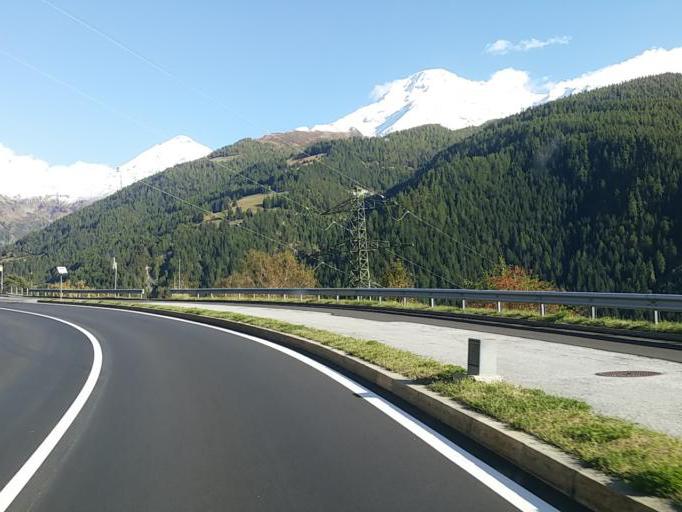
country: CH
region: Valais
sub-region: Brig District
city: Brig
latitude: 46.2939
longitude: 8.0224
